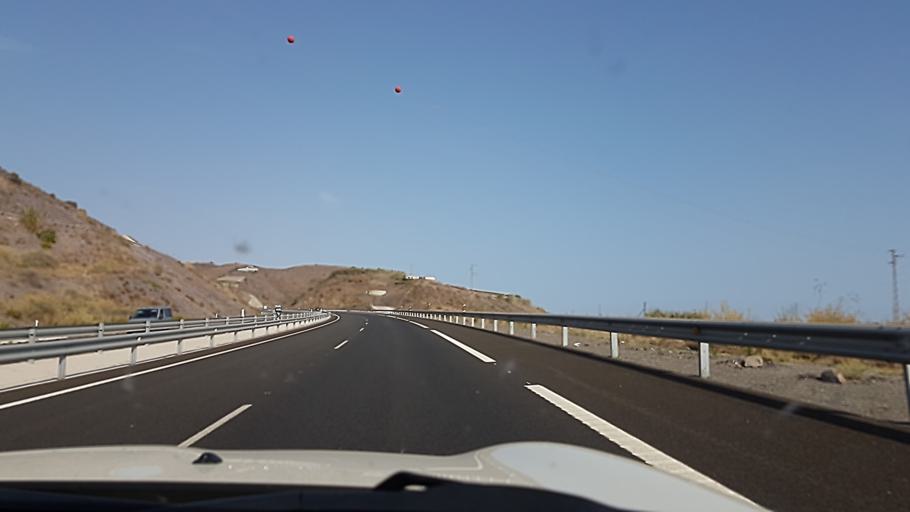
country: ES
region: Andalusia
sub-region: Provincia de Granada
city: Albunol
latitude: 36.7559
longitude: -3.2317
